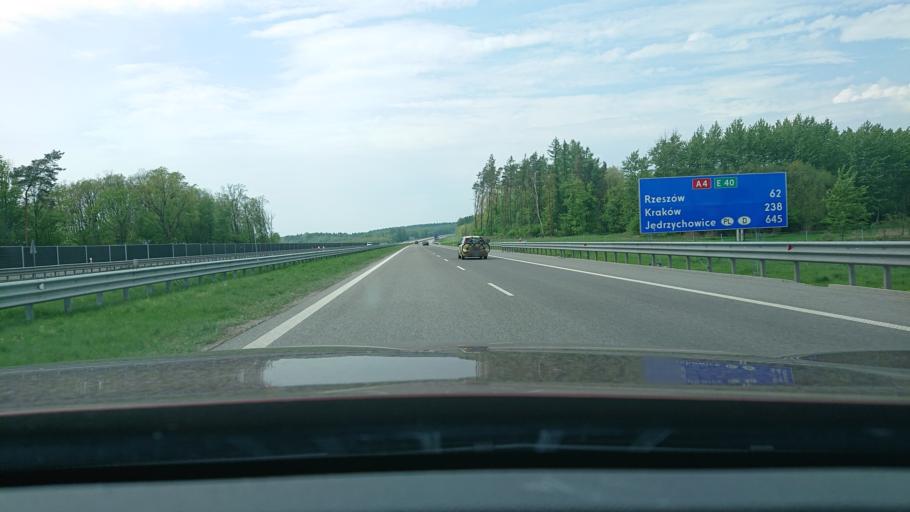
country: PL
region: Subcarpathian Voivodeship
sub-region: Powiat jaroslawski
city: Pawlosiow
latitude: 49.9786
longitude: 22.6312
